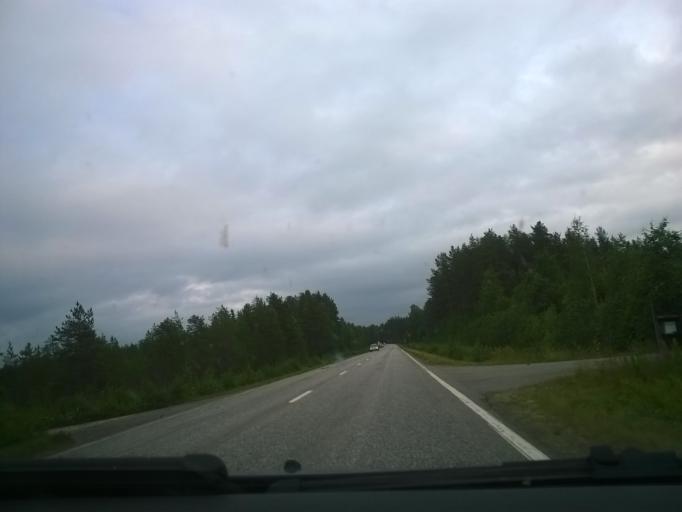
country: FI
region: Kainuu
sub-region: Kehys-Kainuu
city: Kuhmo
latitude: 64.1413
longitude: 29.4409
